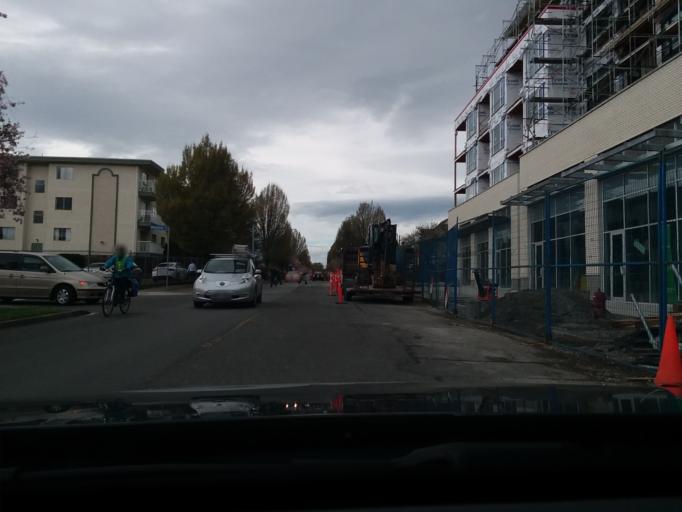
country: CA
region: British Columbia
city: Victoria
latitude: 48.4278
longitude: -123.3561
